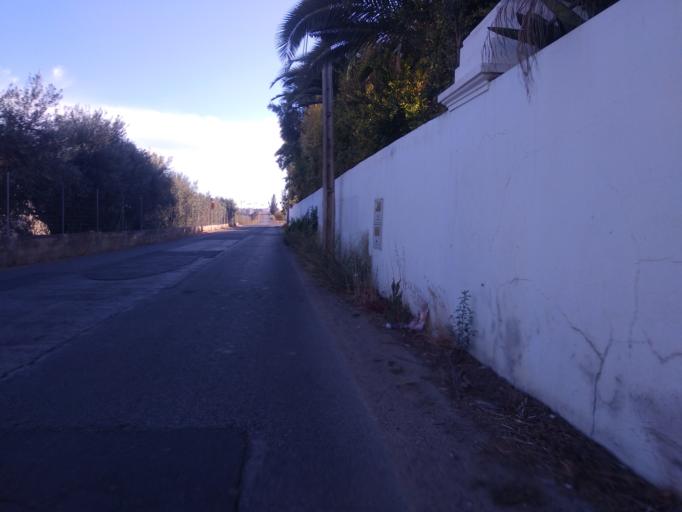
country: PT
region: Faro
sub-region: Faro
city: Faro
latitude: 37.0463
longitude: -7.9377
